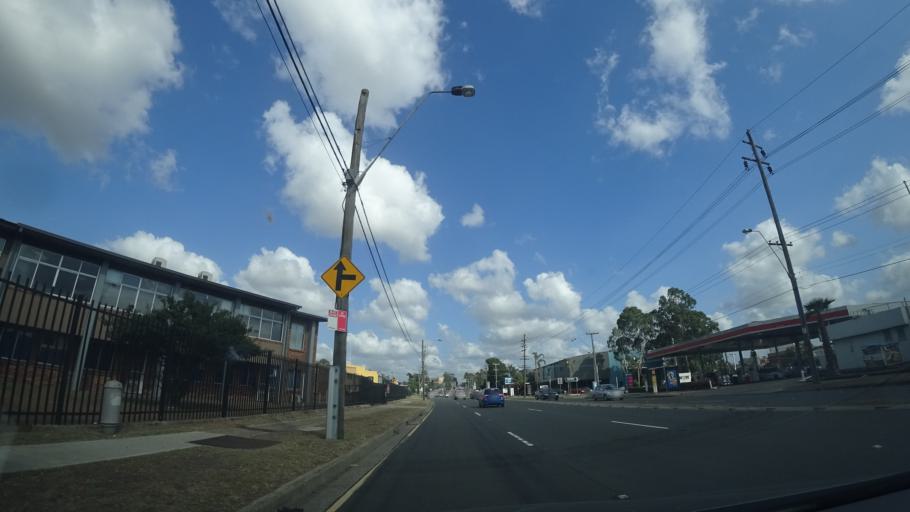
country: AU
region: New South Wales
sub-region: Fairfield
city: Liverpool
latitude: -33.9284
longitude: 150.9336
